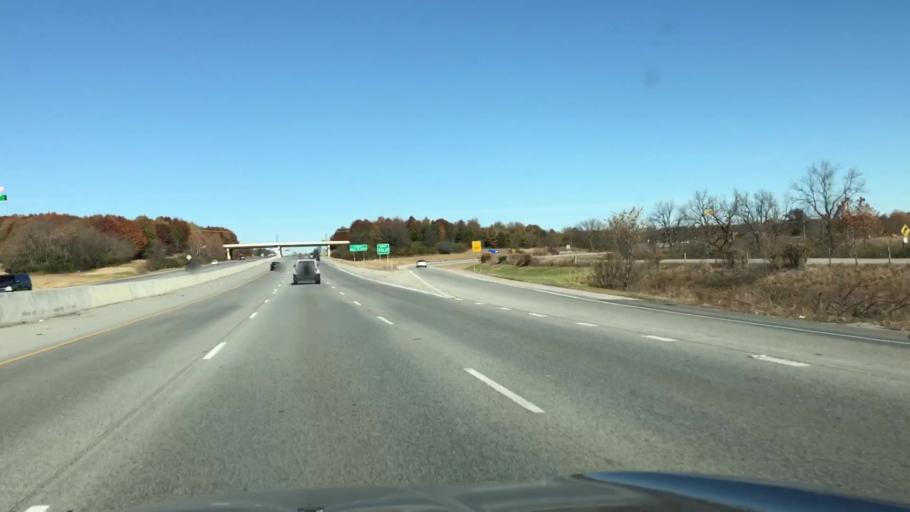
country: US
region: Arkansas
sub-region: Benton County
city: Lowell
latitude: 36.2502
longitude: -94.1504
